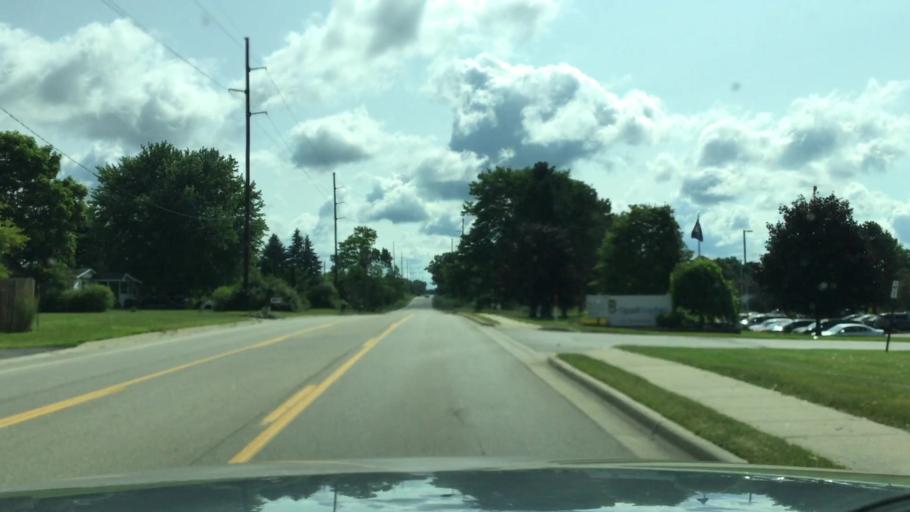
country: US
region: Michigan
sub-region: Montcalm County
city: Greenville
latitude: 43.1923
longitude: -85.2327
